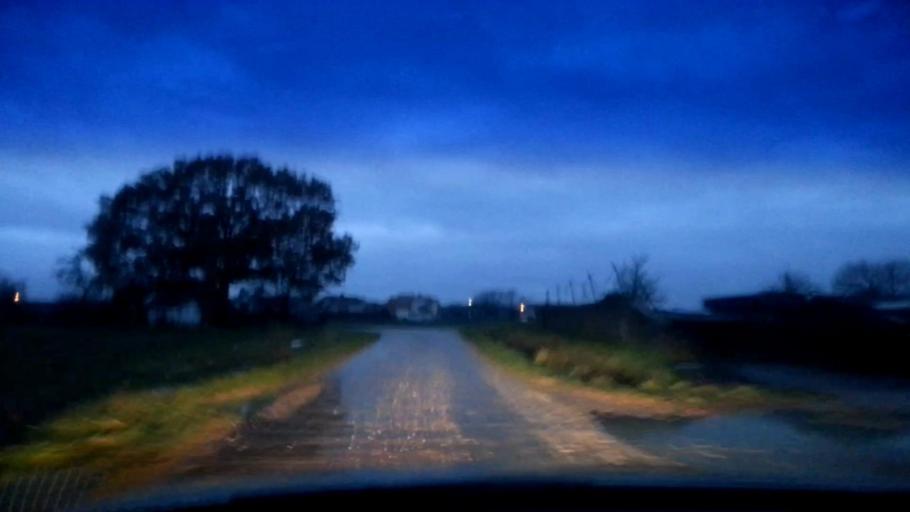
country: DE
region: Bavaria
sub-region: Upper Franconia
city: Memmelsdorf
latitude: 49.9621
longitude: 10.9583
